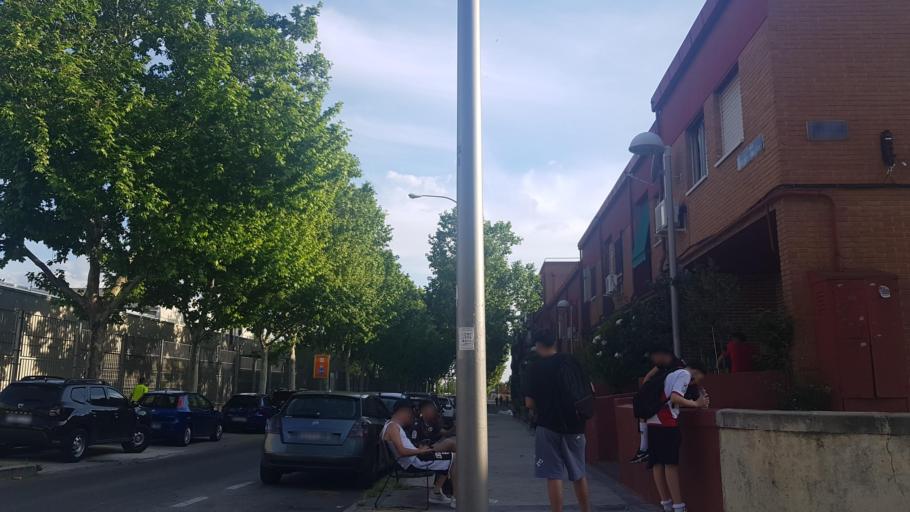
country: ES
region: Madrid
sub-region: Provincia de Madrid
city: Puente de Vallecas
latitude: 40.3725
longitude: -3.6569
